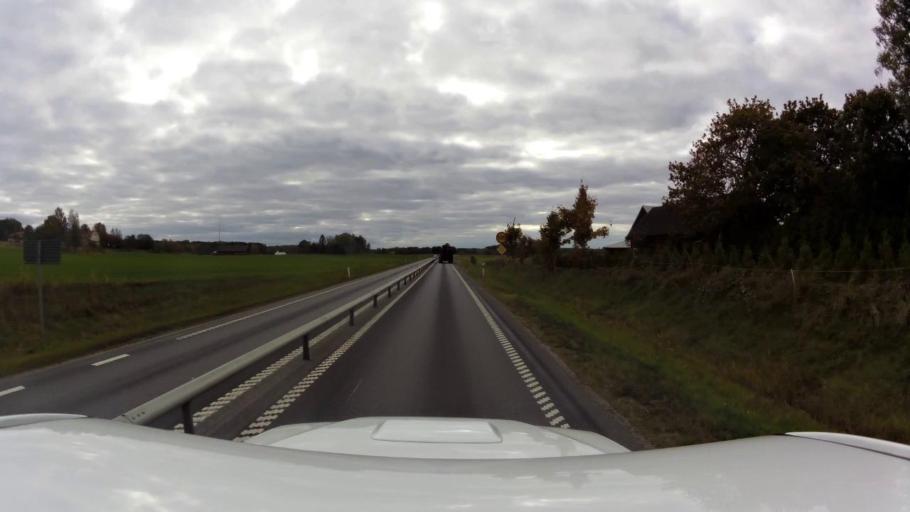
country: SE
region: OEstergoetland
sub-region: Linkopings Kommun
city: Malmslatt
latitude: 58.3346
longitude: 15.5586
